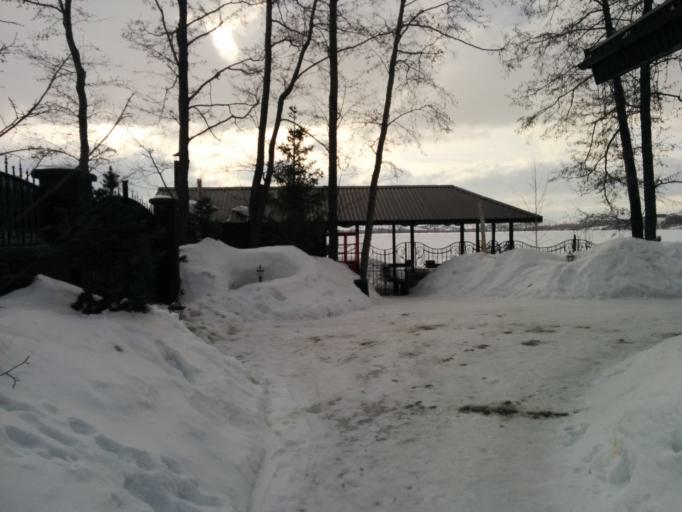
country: RU
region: Bashkortostan
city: Abzakovo
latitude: 53.5959
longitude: 58.6071
